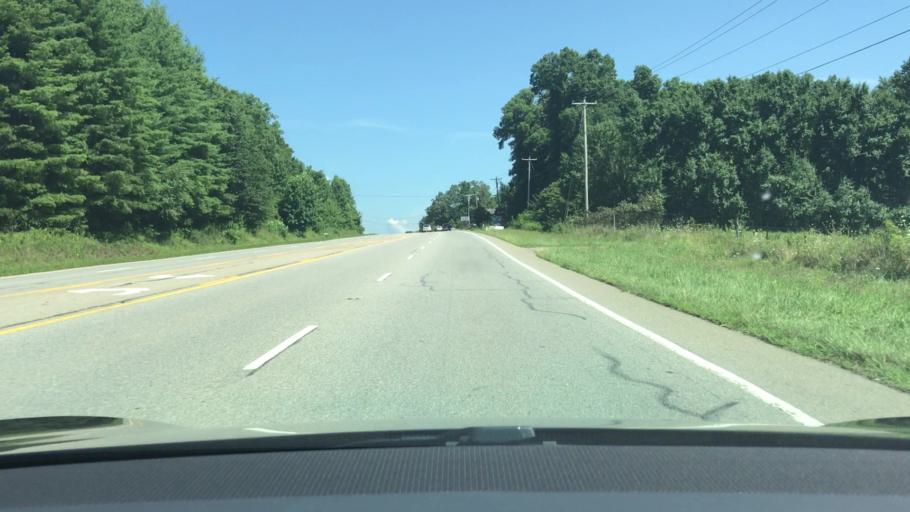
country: US
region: North Carolina
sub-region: Macon County
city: Franklin
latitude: 35.1018
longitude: -83.3855
